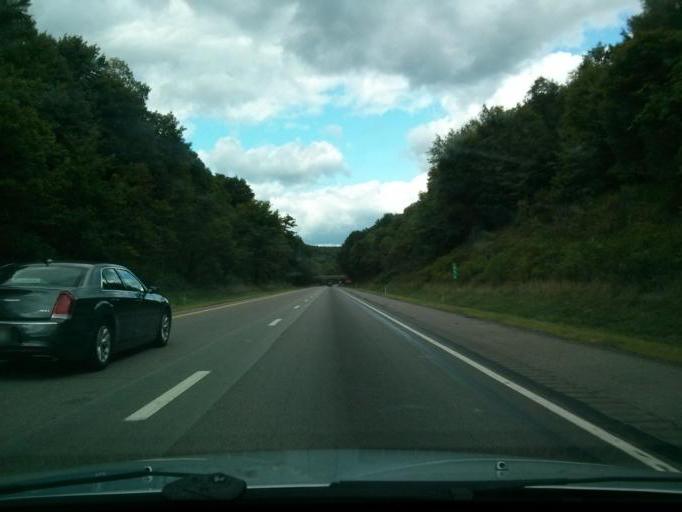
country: US
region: Pennsylvania
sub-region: Jefferson County
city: Brookville
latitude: 41.1444
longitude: -78.9839
